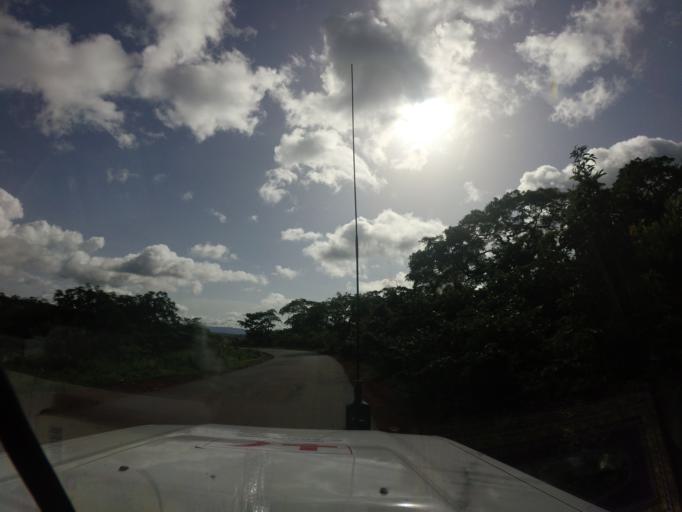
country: GN
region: Mamou
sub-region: Mamou Prefecture
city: Mamou
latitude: 10.2949
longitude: -12.3214
